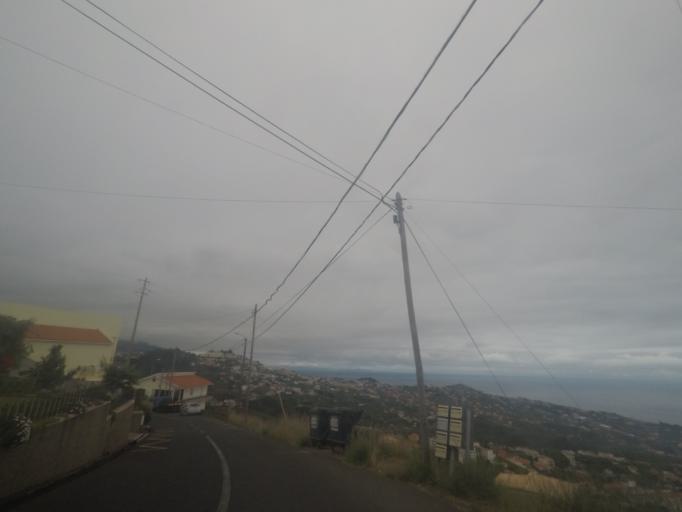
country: PT
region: Madeira
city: Camara de Lobos
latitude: 32.6666
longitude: -16.9678
